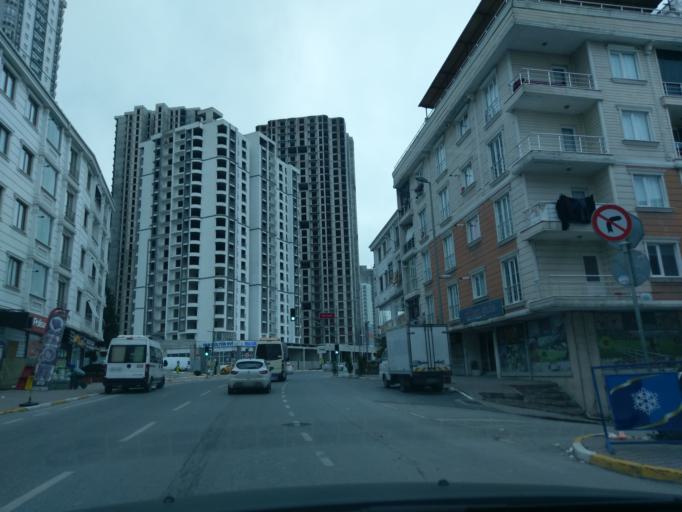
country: TR
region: Istanbul
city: Esenyurt
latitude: 41.0196
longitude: 28.6715
